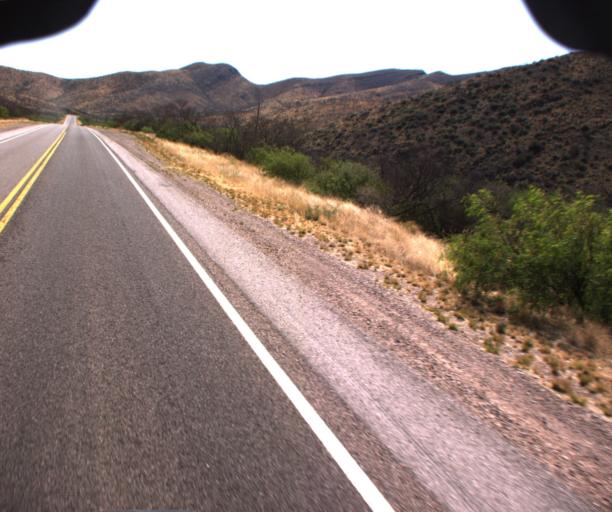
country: US
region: Arizona
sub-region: Cochise County
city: Bisbee
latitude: 31.4315
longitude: -109.8537
